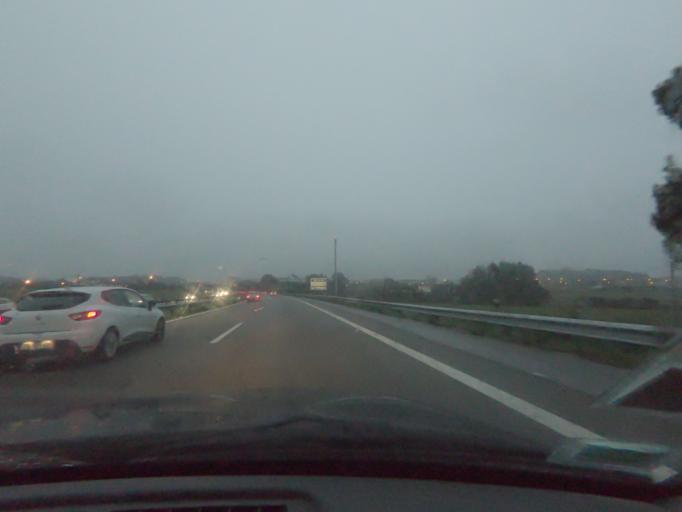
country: PT
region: Porto
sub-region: Matosinhos
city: Lavra
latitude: 41.2559
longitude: -8.7014
